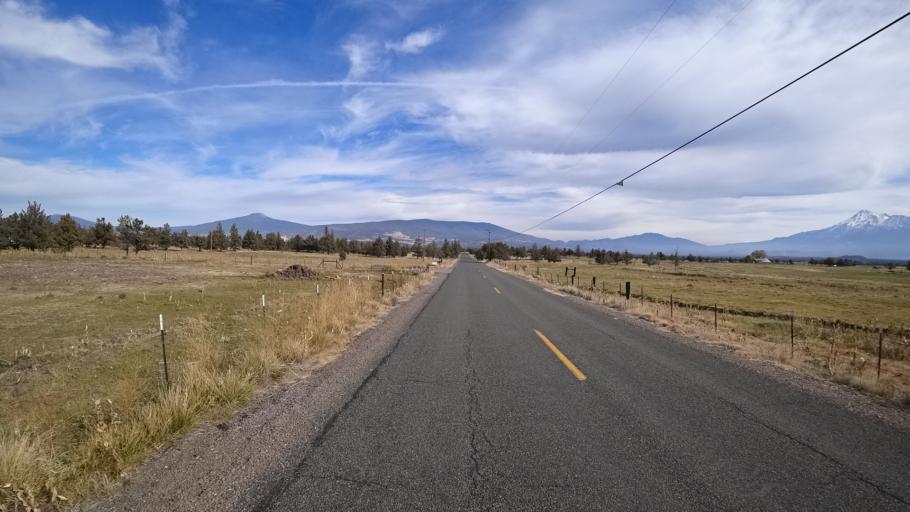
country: US
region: California
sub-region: Siskiyou County
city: Montague
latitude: 41.6384
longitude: -122.4050
